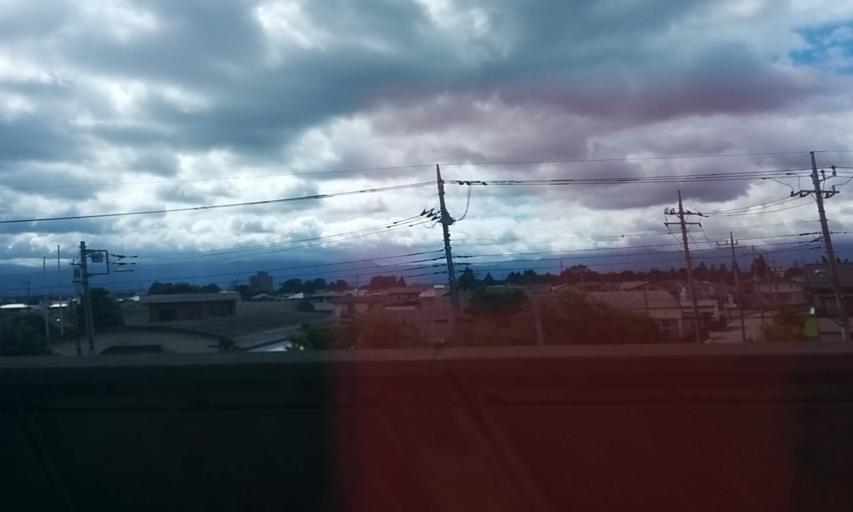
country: JP
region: Tochigi
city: Otawara
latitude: 36.8951
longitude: 139.9943
